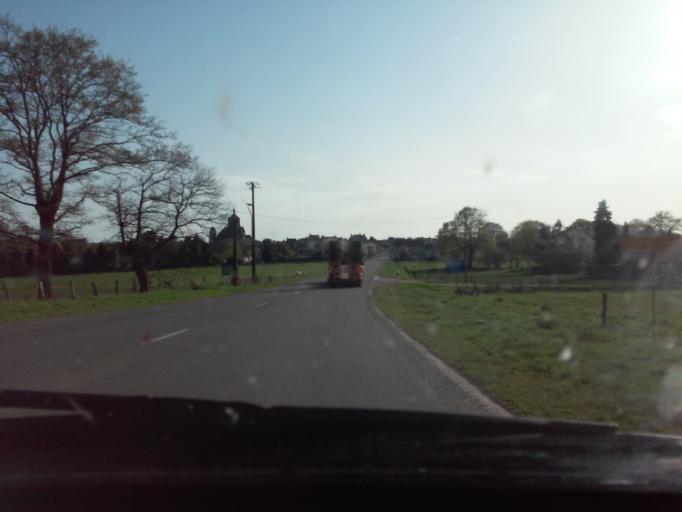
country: FR
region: Brittany
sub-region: Departement d'Ille-et-Vilaine
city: Saint-Aubin-du-Cormier
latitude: 48.2663
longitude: -1.3941
